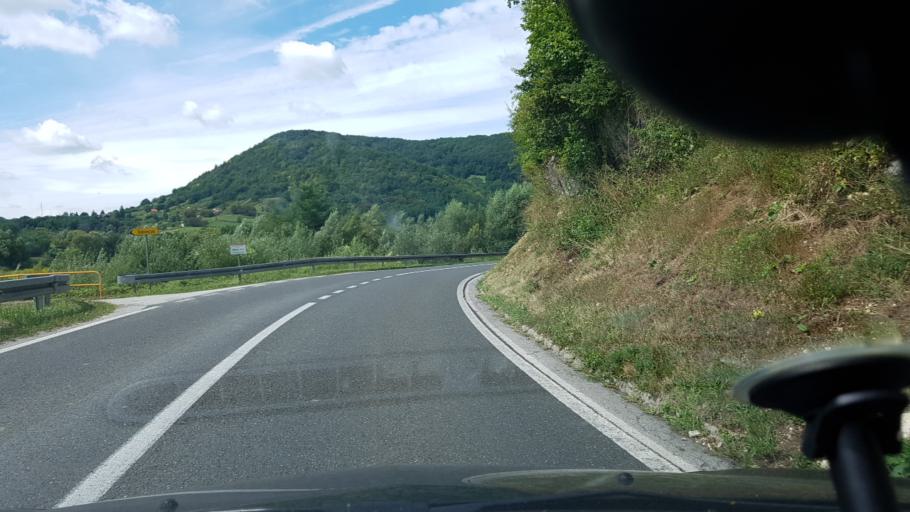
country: HR
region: Varazdinska
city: Lepoglava
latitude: 46.2120
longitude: 16.0002
